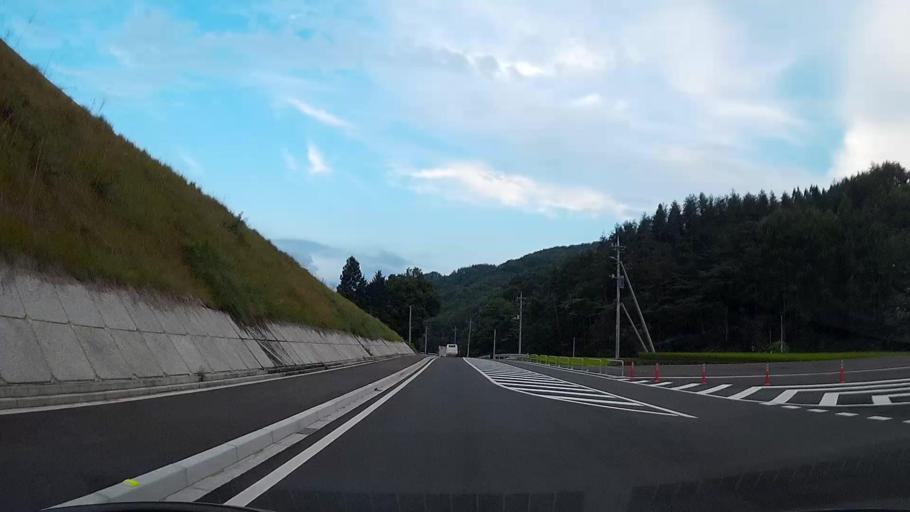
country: JP
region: Gunma
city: Nakanojomachi
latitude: 36.5286
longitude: 138.7204
